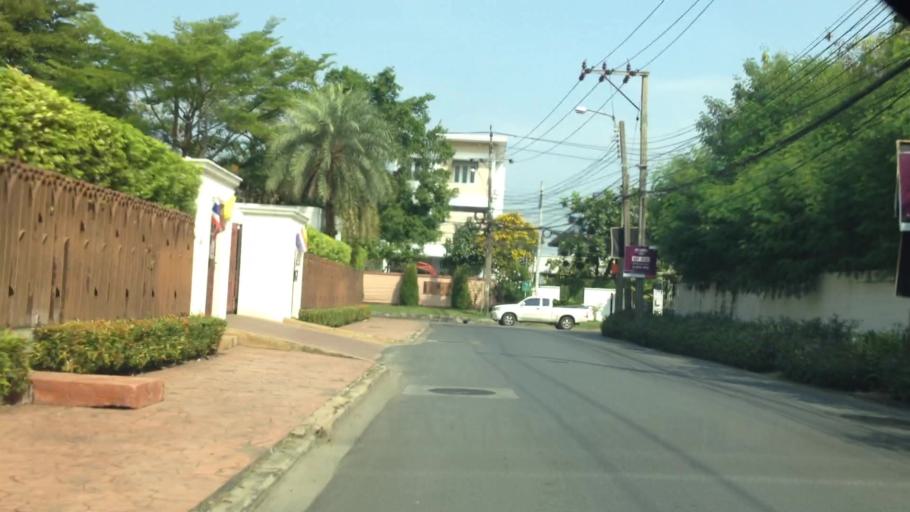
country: TH
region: Bangkok
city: Bang Na
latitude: 13.6855
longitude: 100.6557
